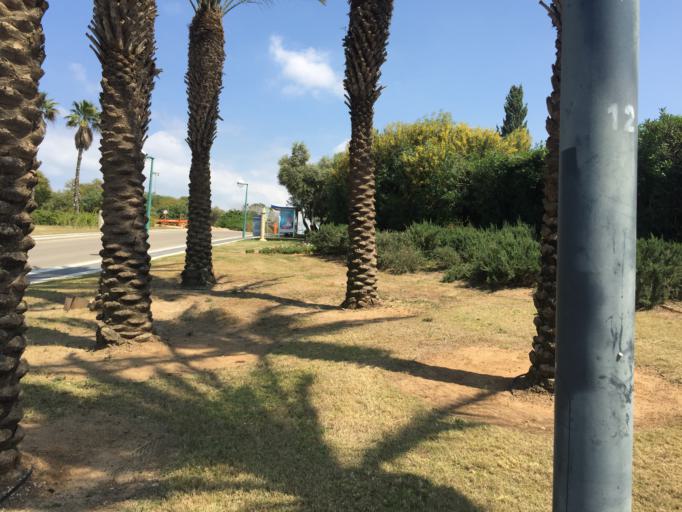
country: IL
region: Haifa
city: Qesarya
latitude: 32.4963
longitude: 34.9040
